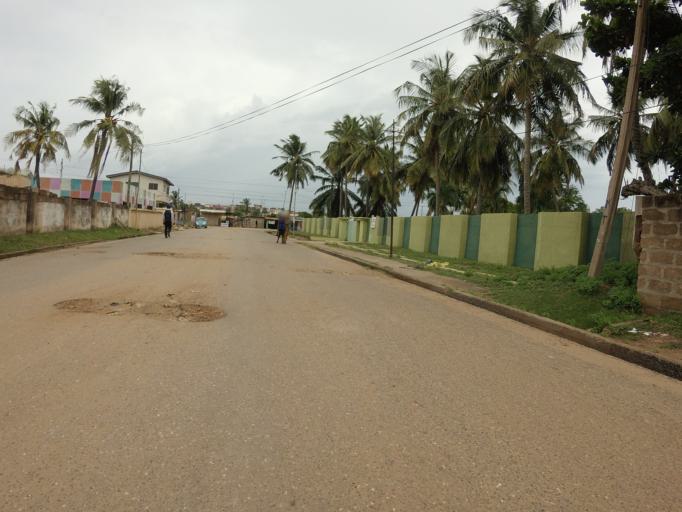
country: GH
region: Greater Accra
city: Accra
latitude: 5.6032
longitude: -0.2095
